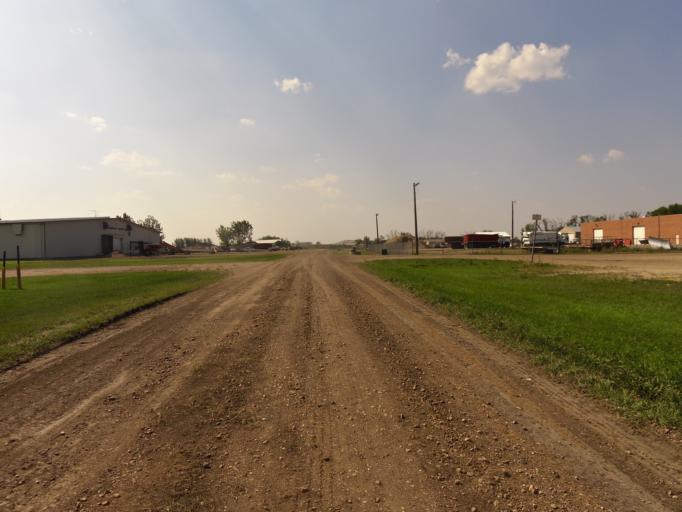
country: US
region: North Dakota
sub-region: Walsh County
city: Grafton
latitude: 48.4326
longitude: -97.4002
